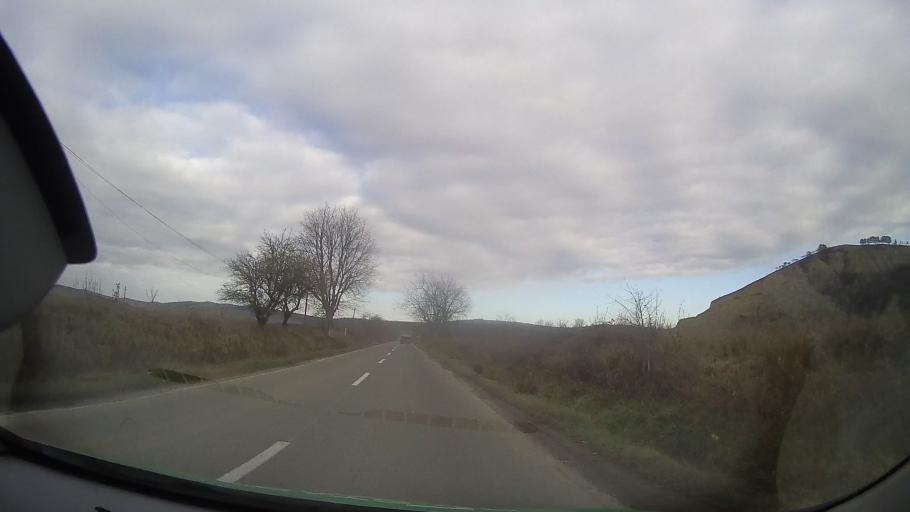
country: RO
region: Mures
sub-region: Comuna Iernut
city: Iernut
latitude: 46.4645
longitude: 24.2182
